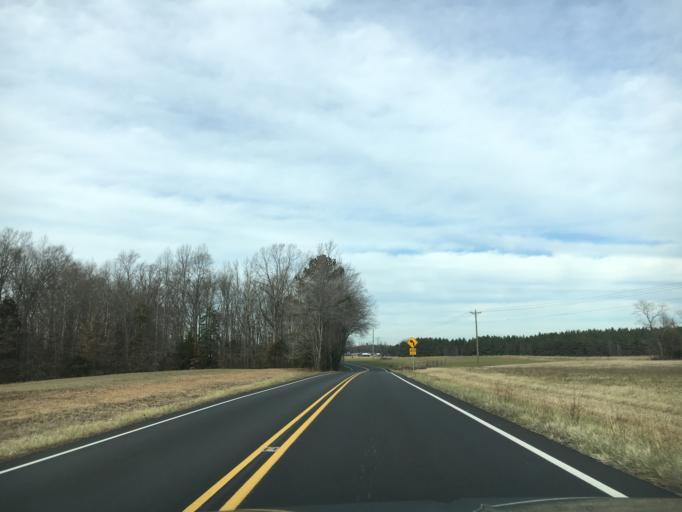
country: US
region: Virginia
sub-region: Goochland County
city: Goochland
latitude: 37.8142
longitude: -77.8709
